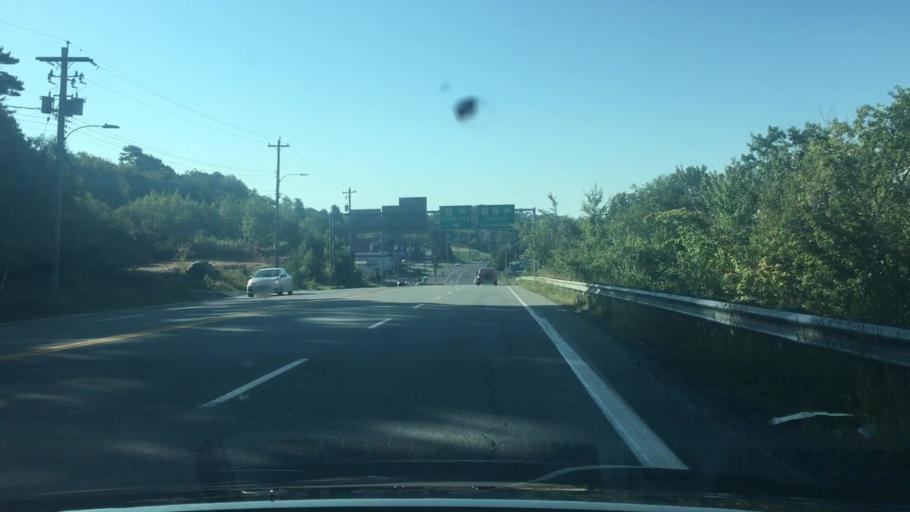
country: CA
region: Nova Scotia
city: Dartmouth
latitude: 44.7423
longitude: -63.6556
